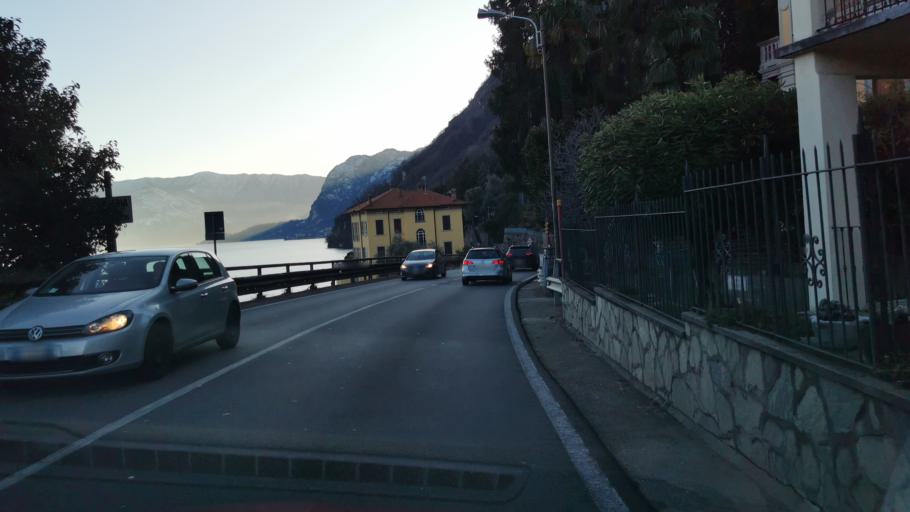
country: IT
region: Lombardy
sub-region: Provincia di Como
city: San Siro
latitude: 46.0522
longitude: 9.2587
